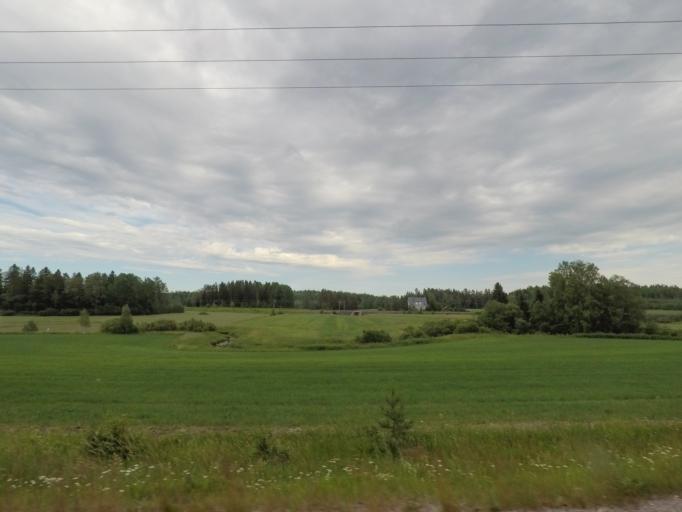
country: FI
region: Uusimaa
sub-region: Helsinki
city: Maentsaelae
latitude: 60.6868
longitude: 25.3707
